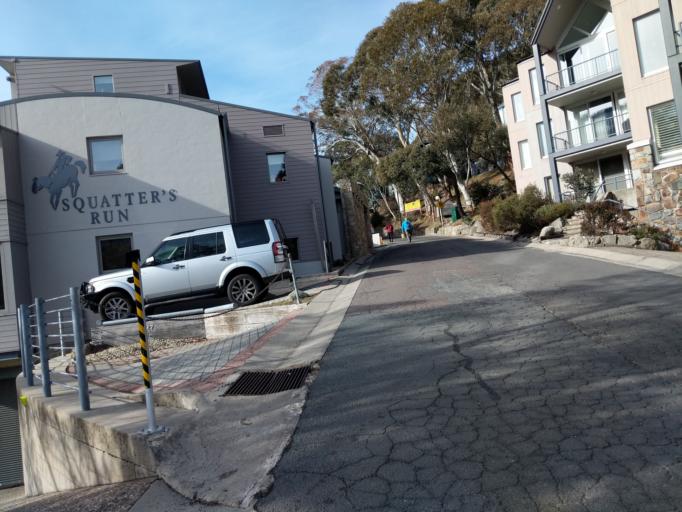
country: AU
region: New South Wales
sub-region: Snowy River
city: Jindabyne
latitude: -36.5048
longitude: 148.3056
